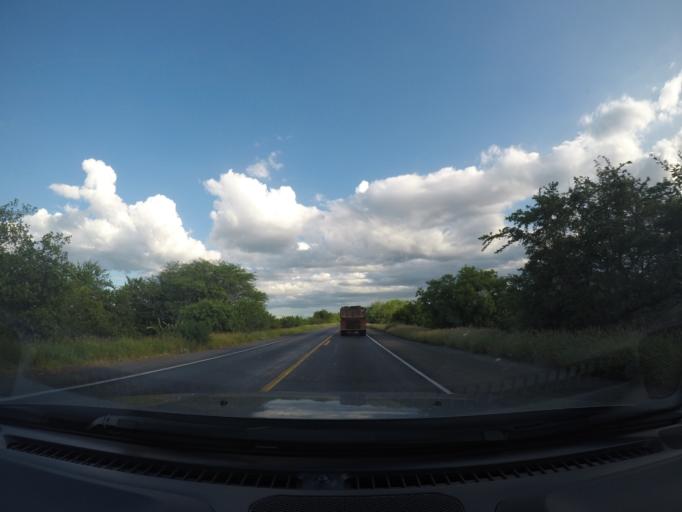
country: BR
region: Bahia
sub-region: Oliveira Dos Brejinhos
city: Beira Rio
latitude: -12.2362
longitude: -42.7754
